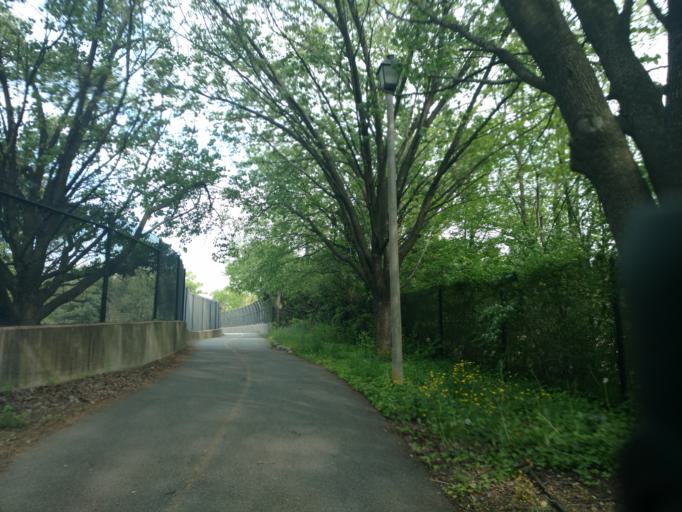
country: US
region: Virginia
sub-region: Arlington County
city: Arlington
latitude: 38.8827
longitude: -77.1200
